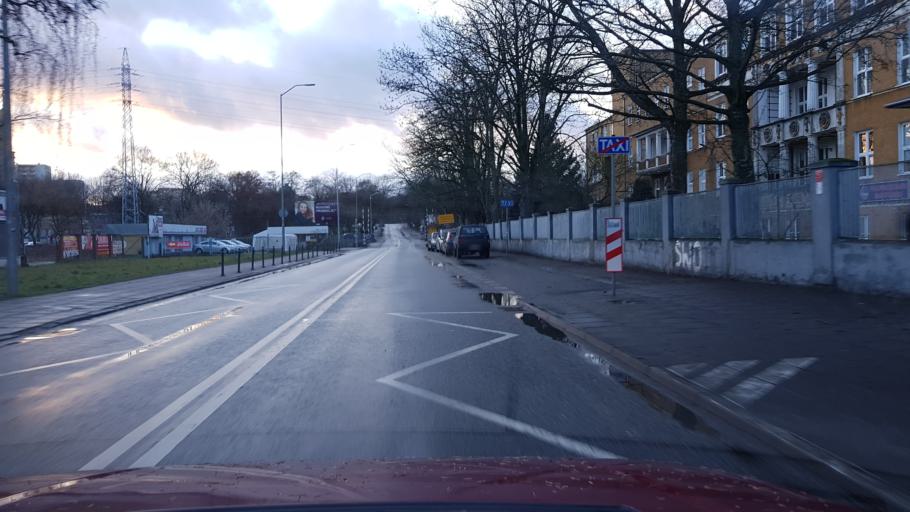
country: PL
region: West Pomeranian Voivodeship
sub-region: Szczecin
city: Szczecin
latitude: 53.4345
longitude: 14.5251
